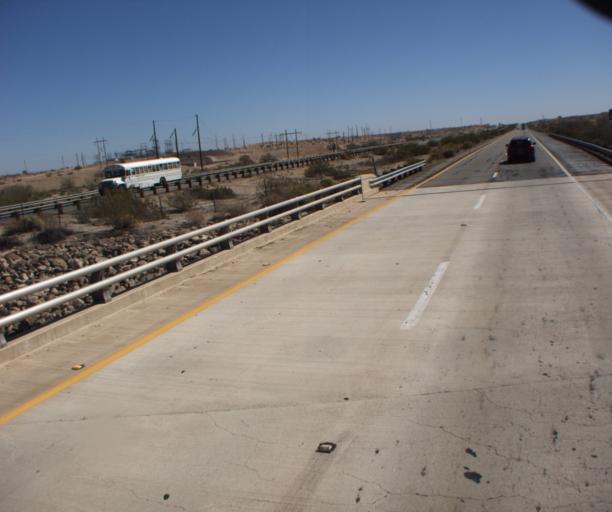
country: US
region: Arizona
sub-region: Yuma County
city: Wellton
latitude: 32.6643
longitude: -114.2731
